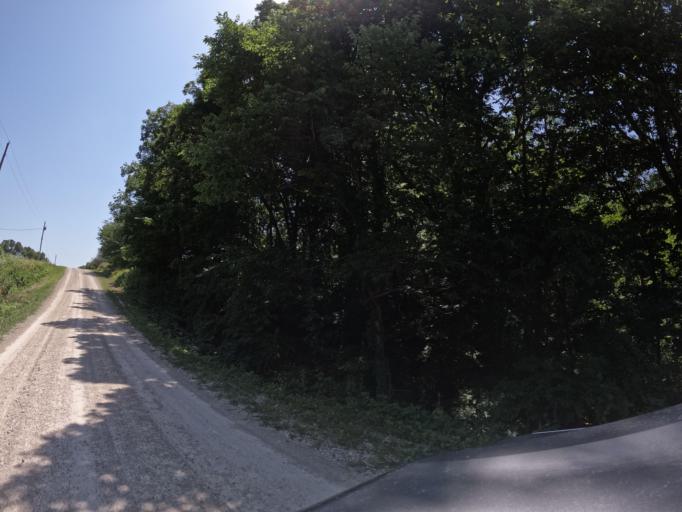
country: US
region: Iowa
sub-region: Henry County
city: Mount Pleasant
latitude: 40.9916
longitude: -91.6363
